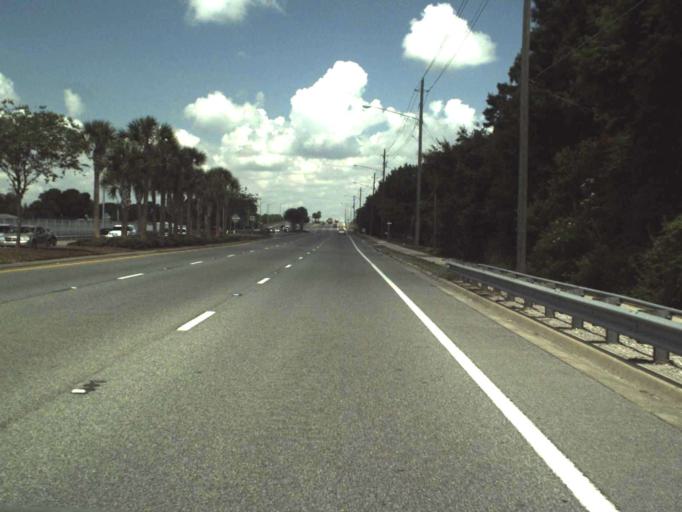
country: US
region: Florida
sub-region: Lake County
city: Tavares
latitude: 28.8135
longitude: -81.7526
